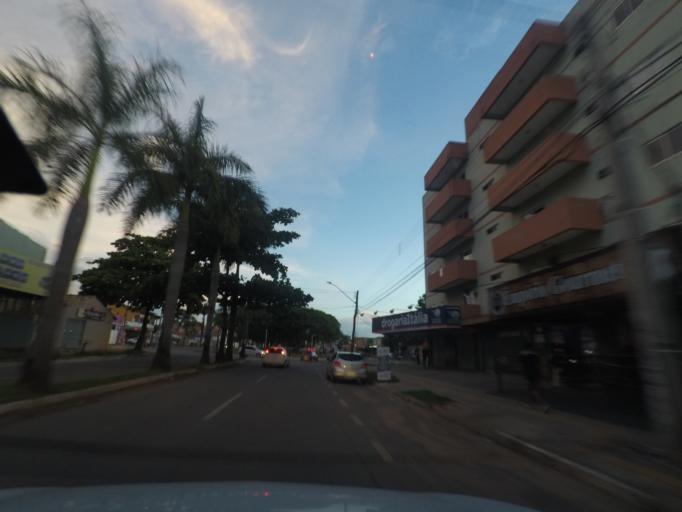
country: BR
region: Goias
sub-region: Goiania
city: Goiania
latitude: -16.7041
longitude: -49.3113
